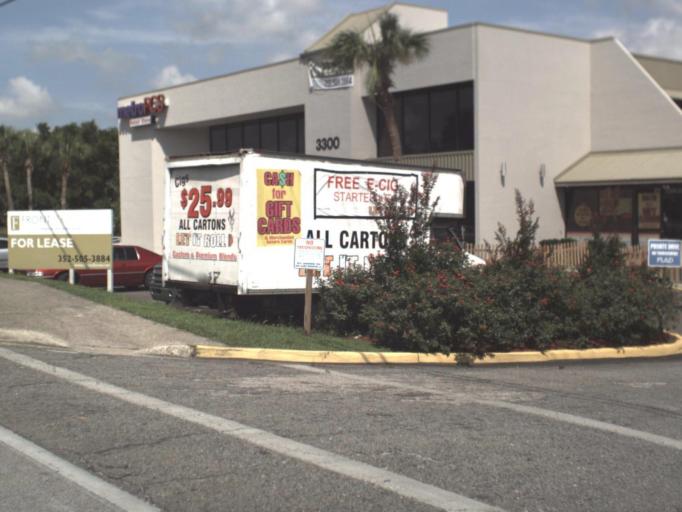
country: US
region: Florida
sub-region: Alachua County
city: Gainesville
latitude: 29.6281
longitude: -82.3708
